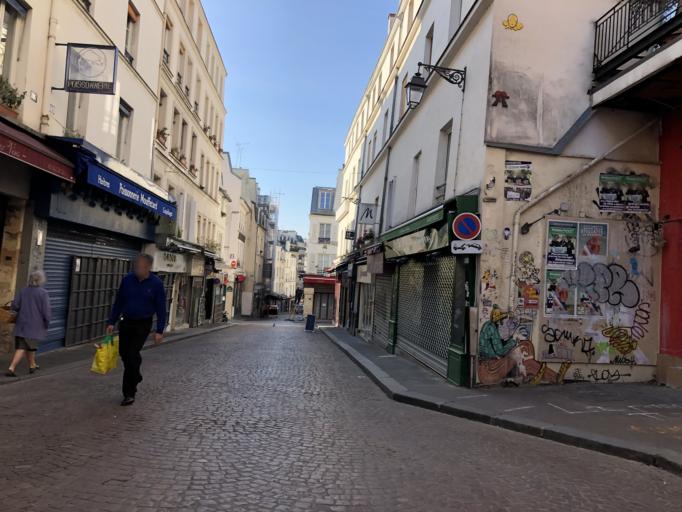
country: FR
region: Ile-de-France
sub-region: Paris
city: Paris
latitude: 48.8409
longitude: 2.3496
